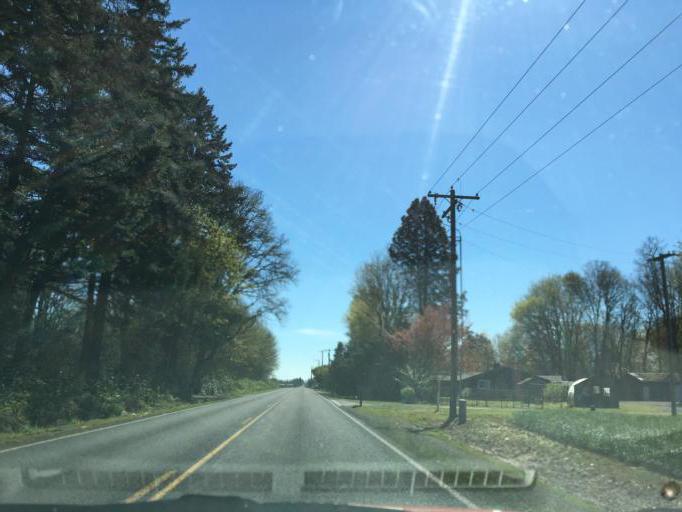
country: US
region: Oregon
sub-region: Clackamas County
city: Canby
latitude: 45.1995
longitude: -122.7227
